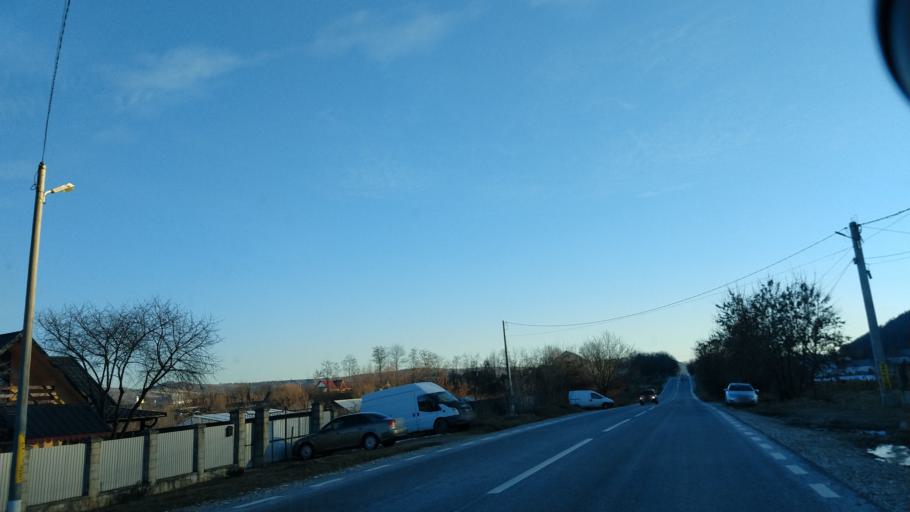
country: RO
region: Bacau
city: Gura Vaii
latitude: 46.3220
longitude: 26.7462
